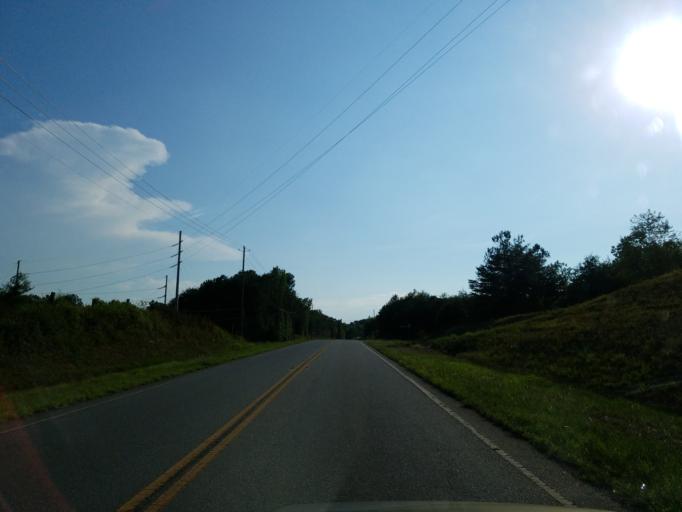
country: US
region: Georgia
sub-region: Bartow County
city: Rydal
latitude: 34.3399
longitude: -84.7252
